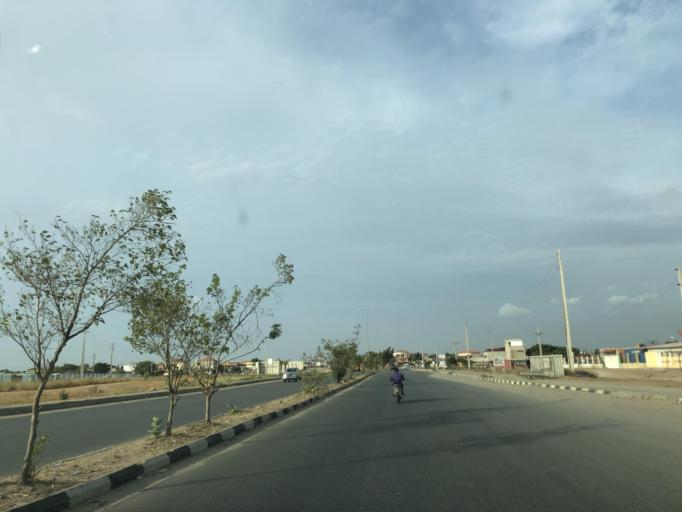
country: AO
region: Luanda
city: Luanda
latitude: -8.9321
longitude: 13.3013
